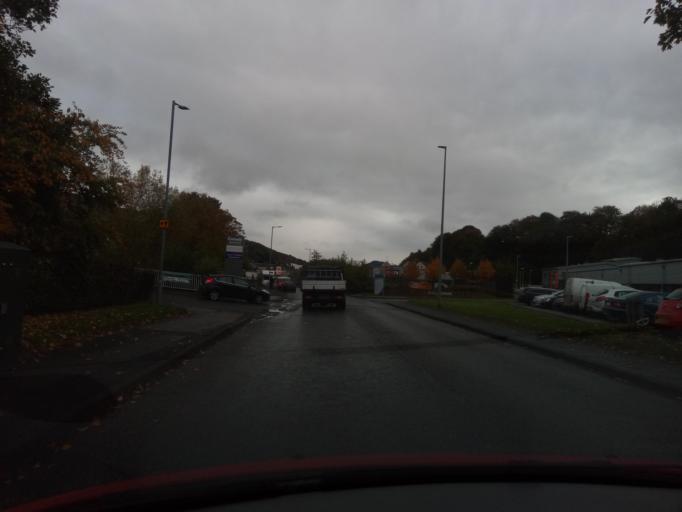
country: GB
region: Scotland
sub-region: The Scottish Borders
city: Galashiels
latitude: 55.6223
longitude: -2.8207
